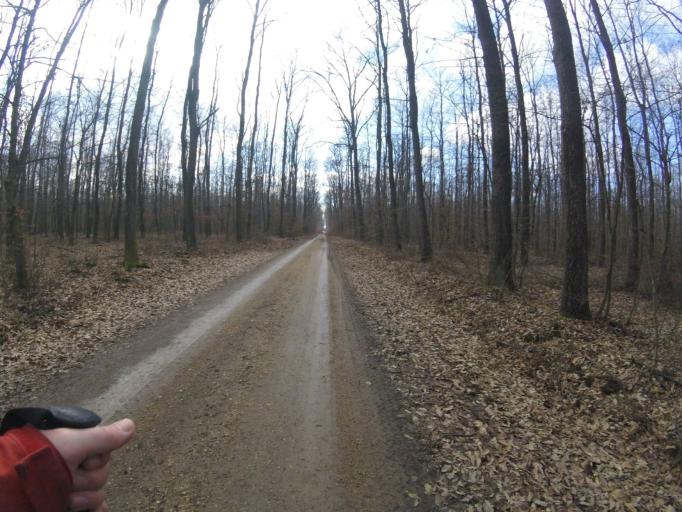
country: HU
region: Zala
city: Turje
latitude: 47.0714
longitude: 17.0089
